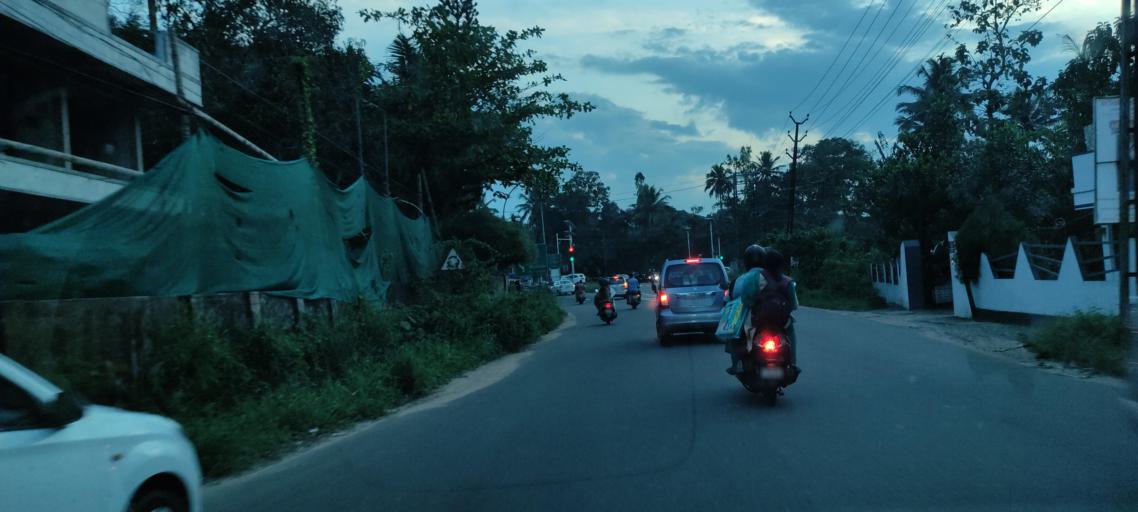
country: IN
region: Kerala
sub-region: Pattanamtitta
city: Adur
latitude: 9.1471
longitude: 76.7325
